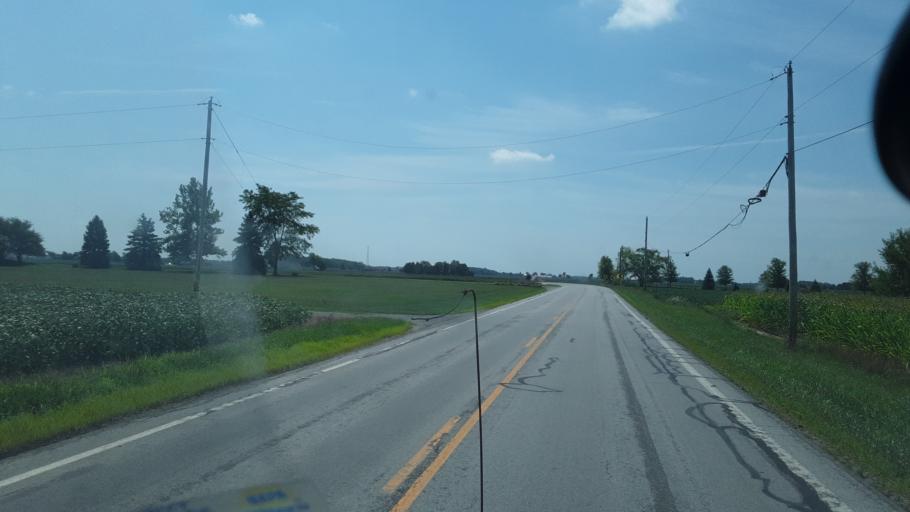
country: US
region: Ohio
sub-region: Hancock County
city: Arlington
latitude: 40.9431
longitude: -83.5750
